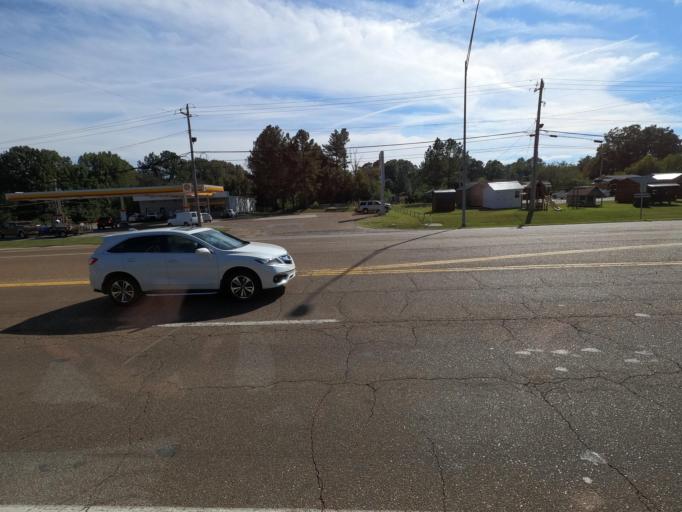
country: US
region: Tennessee
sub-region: Fayette County
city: Hickory Withe
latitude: 35.2102
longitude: -89.6515
